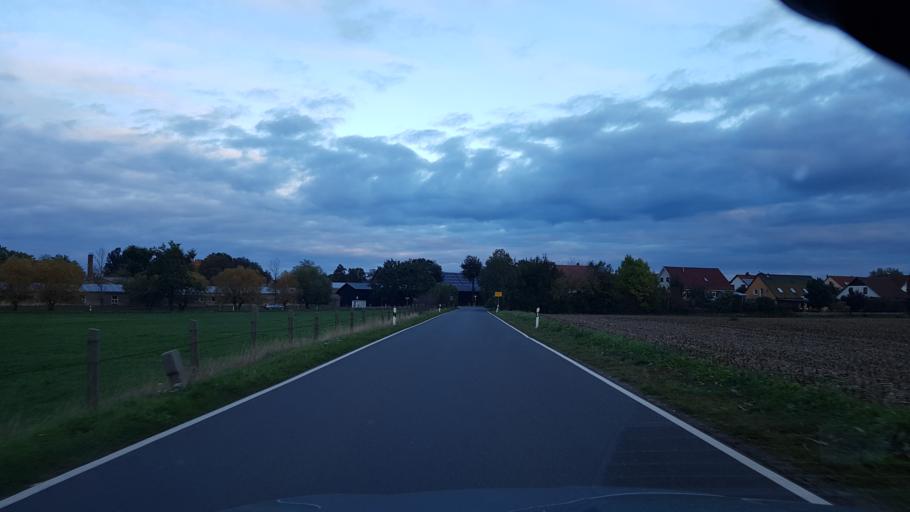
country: DE
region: Saxony
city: Ebersbach
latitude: 51.2790
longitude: 13.6209
